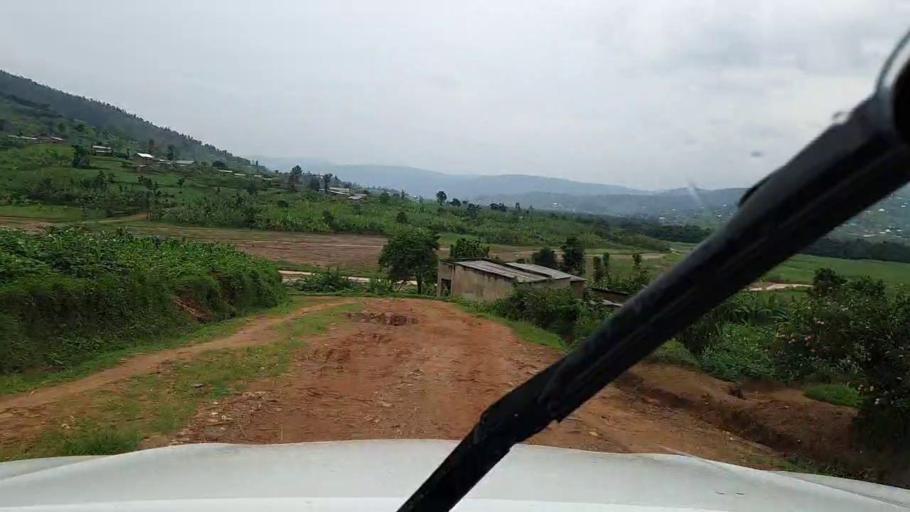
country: RW
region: Kigali
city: Kigali
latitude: -1.8967
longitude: 29.9530
